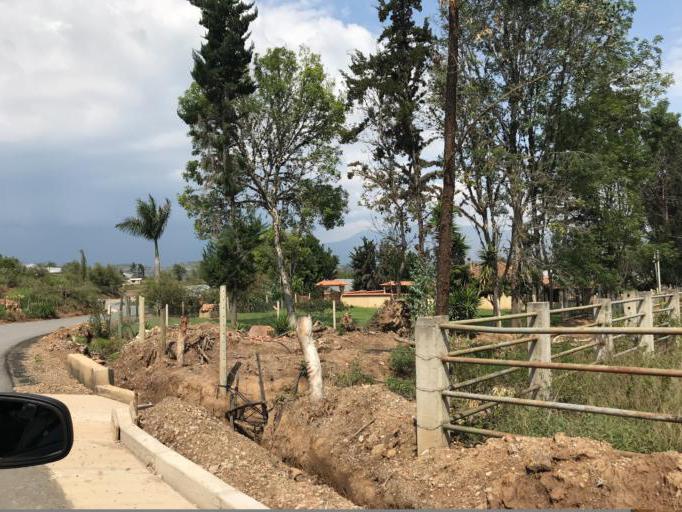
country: CO
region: Boyaca
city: Sutamarchan
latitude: 5.6289
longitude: -73.6116
